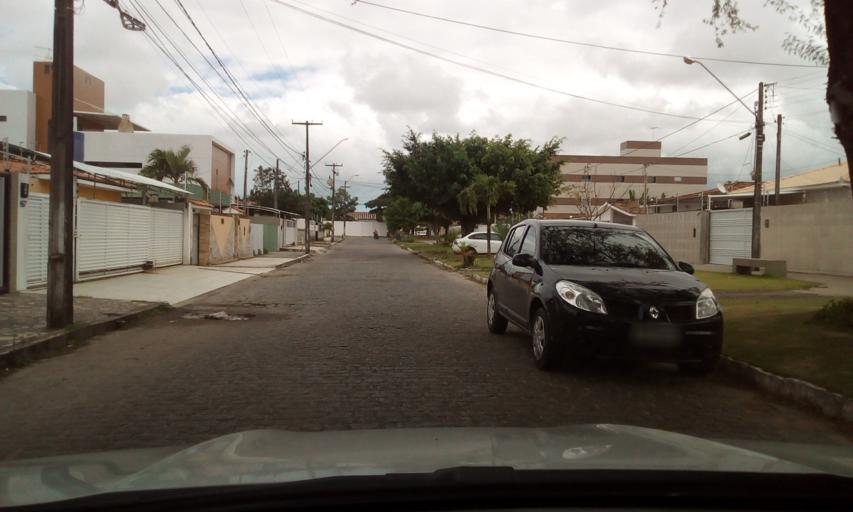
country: BR
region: Paraiba
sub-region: Joao Pessoa
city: Joao Pessoa
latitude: -7.1565
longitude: -34.8751
